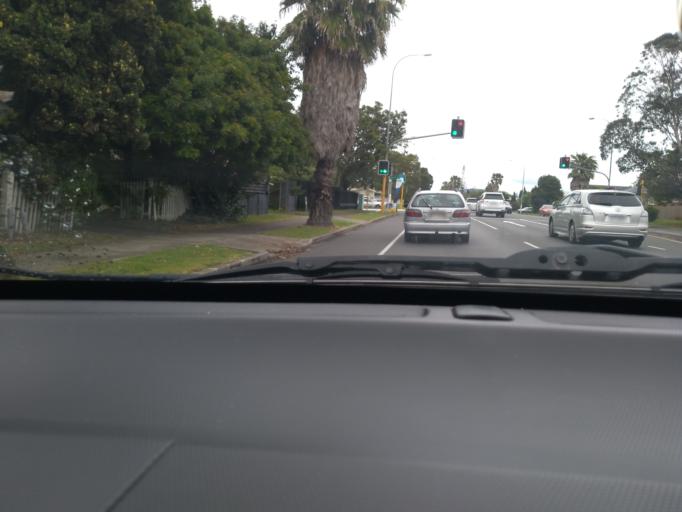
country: NZ
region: Auckland
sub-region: Auckland
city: Tamaki
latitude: -36.9208
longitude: 174.8777
